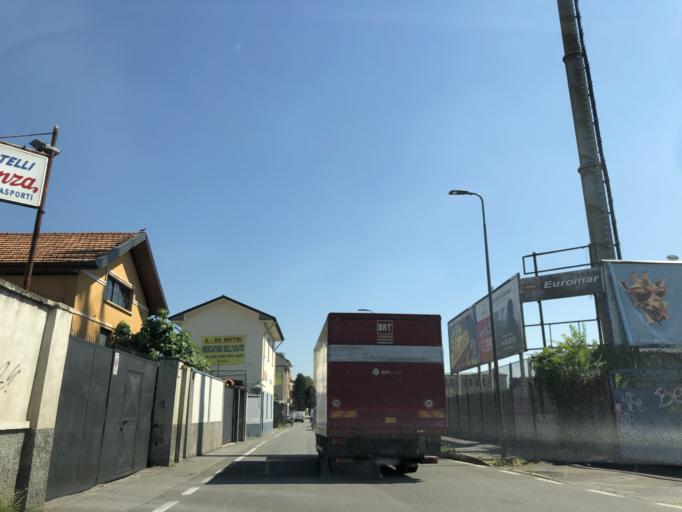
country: IT
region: Lombardy
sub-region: Citta metropolitana di Milano
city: Cormano
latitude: 45.5111
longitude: 9.1668
